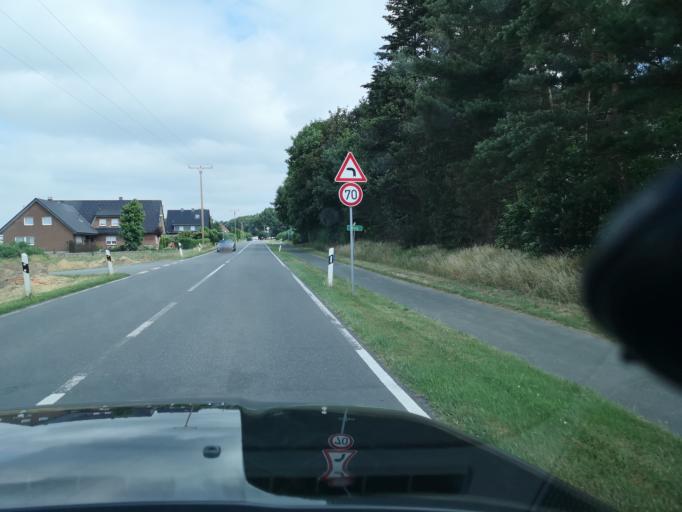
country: DE
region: North Rhine-Westphalia
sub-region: Regierungsbezirk Dusseldorf
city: Hamminkeln
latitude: 51.7490
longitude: 6.6414
